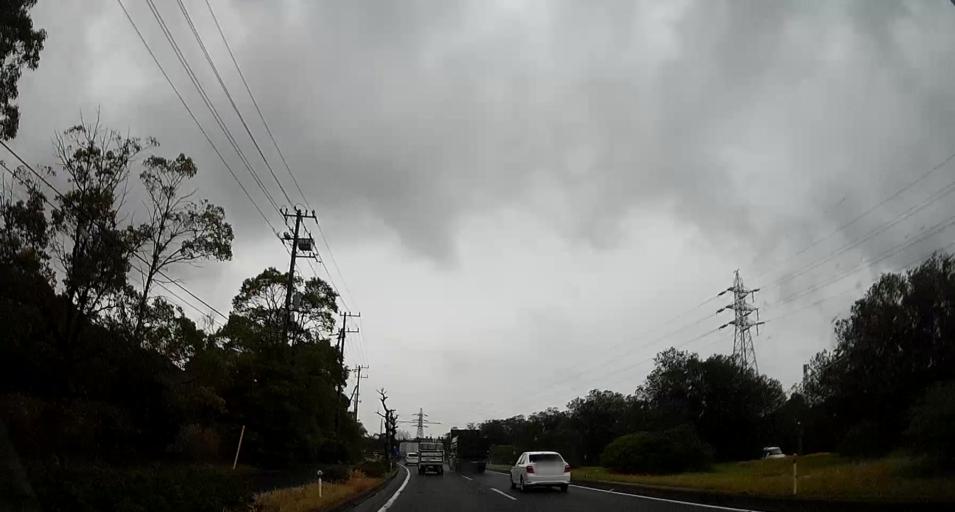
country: JP
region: Chiba
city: Ichihara
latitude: 35.5290
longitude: 140.0688
